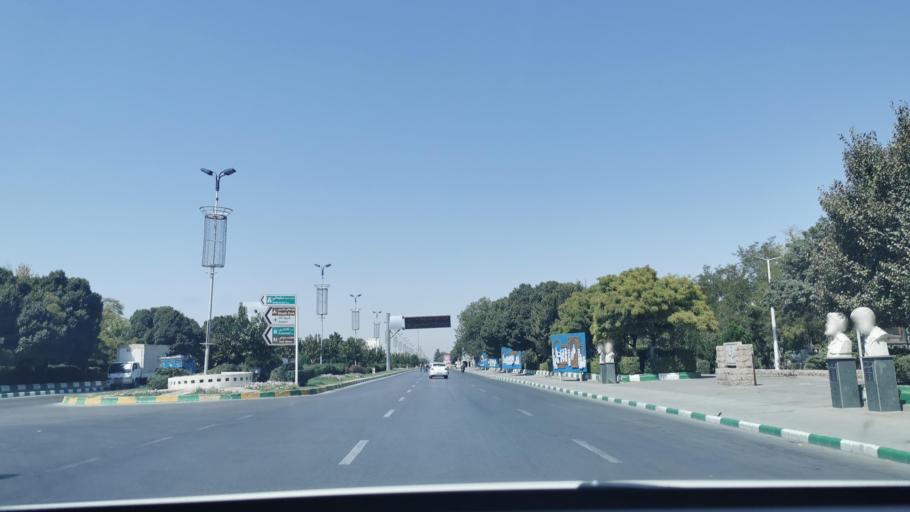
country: IR
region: Razavi Khorasan
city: Mashhad
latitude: 36.2545
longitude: 59.6124
